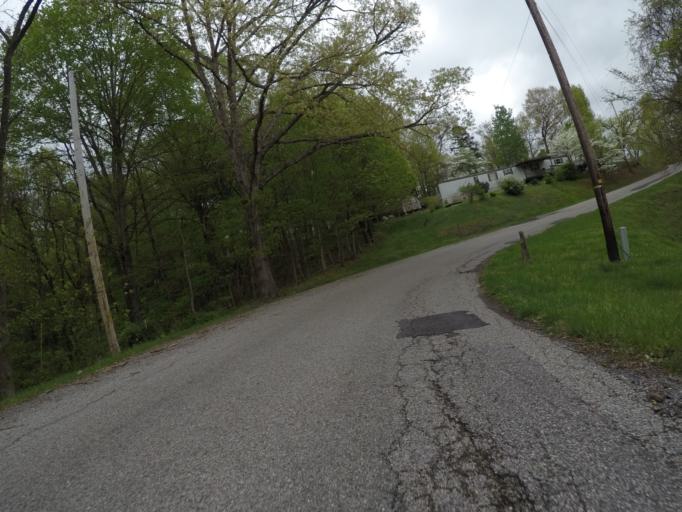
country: US
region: West Virginia
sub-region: Cabell County
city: Barboursville
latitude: 38.3972
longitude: -82.2522
